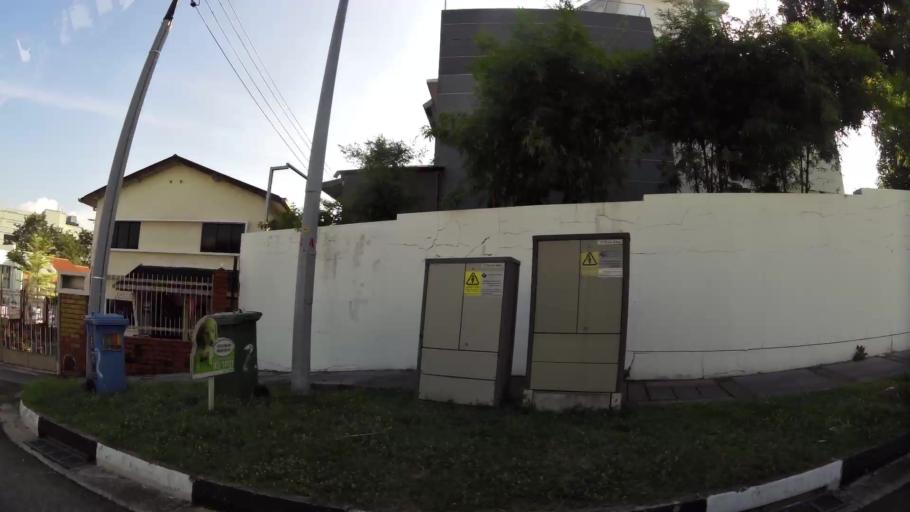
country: SG
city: Singapore
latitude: 1.3207
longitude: 103.9206
